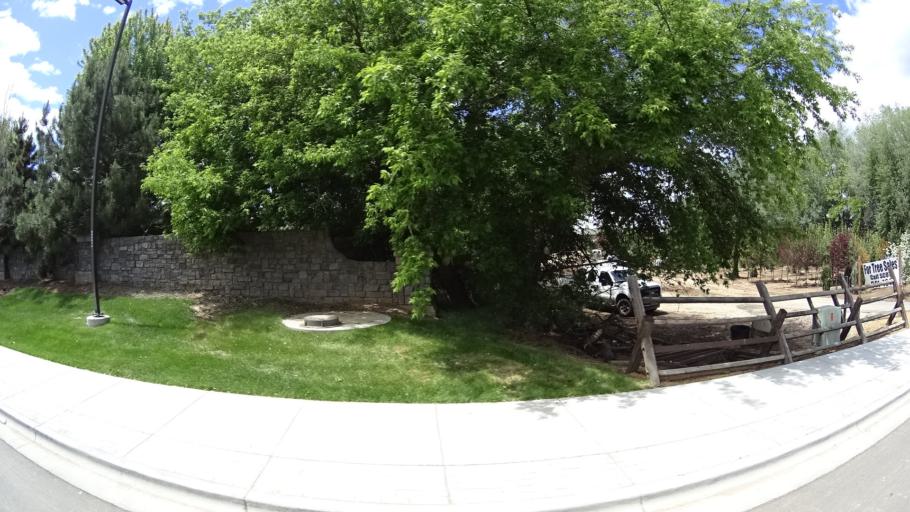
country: US
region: Idaho
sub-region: Ada County
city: Eagle
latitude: 43.6427
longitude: -116.3344
